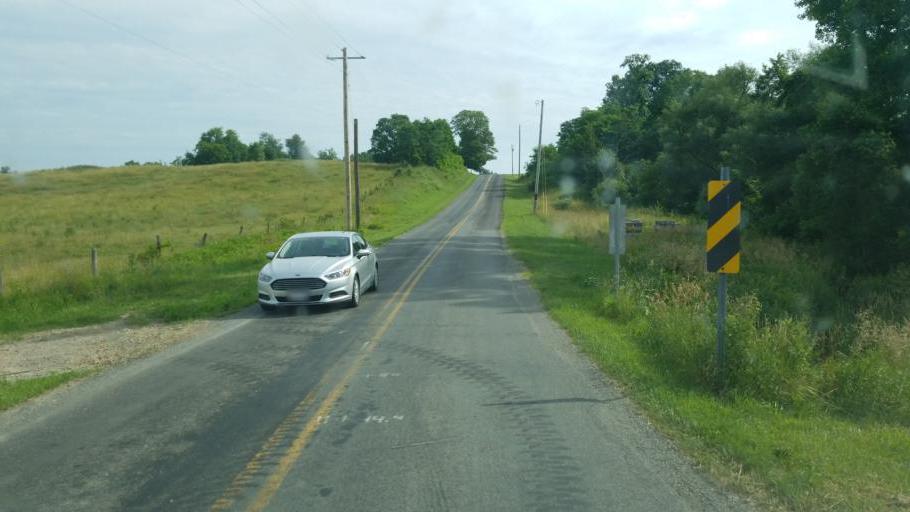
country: US
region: Ohio
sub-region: Medina County
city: Lodi
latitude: 41.0538
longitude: -82.0325
